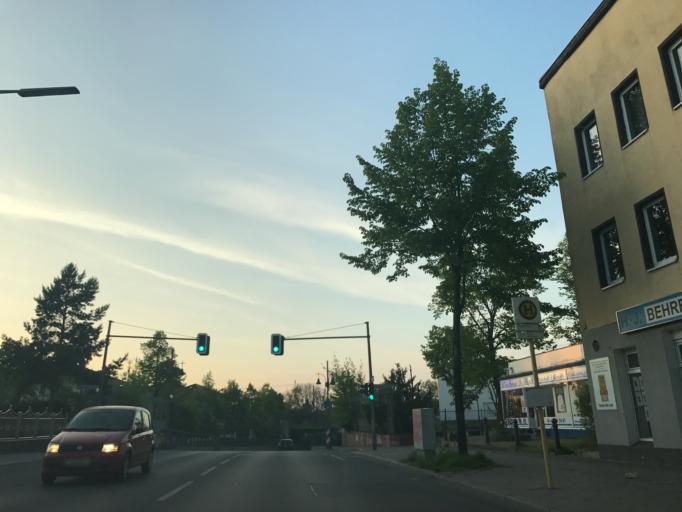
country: DE
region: Berlin
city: Staaken
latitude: 52.5354
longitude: 13.1570
